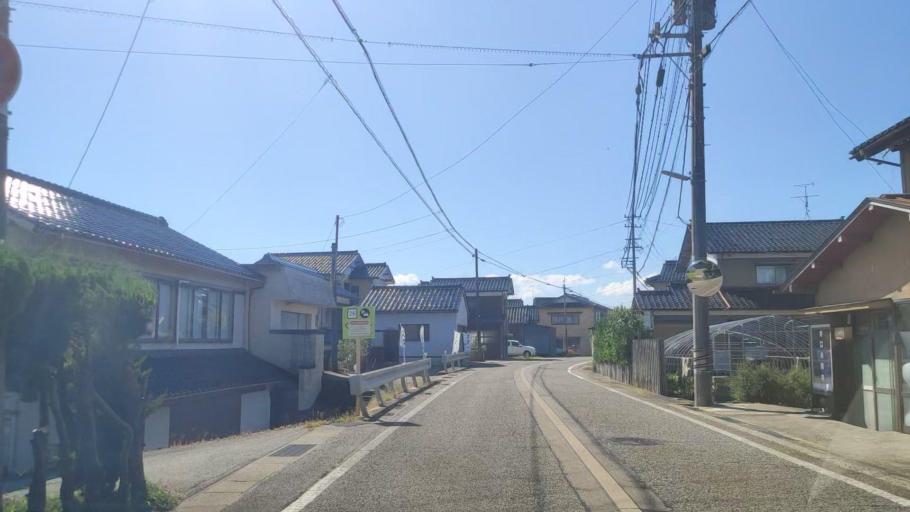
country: JP
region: Ishikawa
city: Nanao
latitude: 37.4427
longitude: 137.2835
